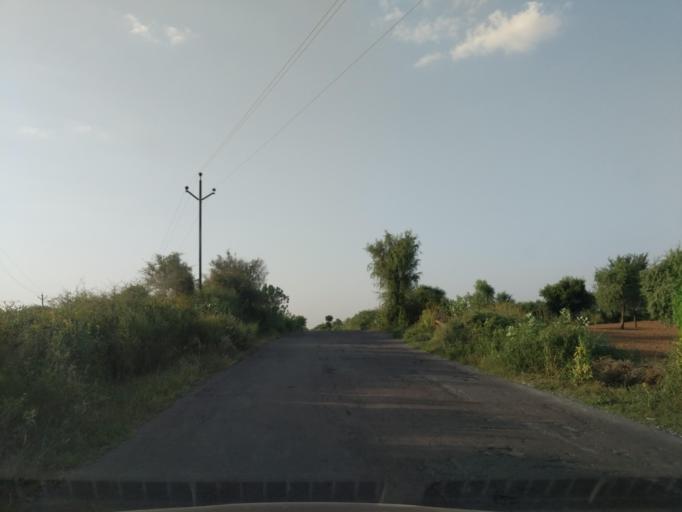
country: IN
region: Rajasthan
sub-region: Churu
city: Rajgarh
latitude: 28.5423
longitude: 75.3725
